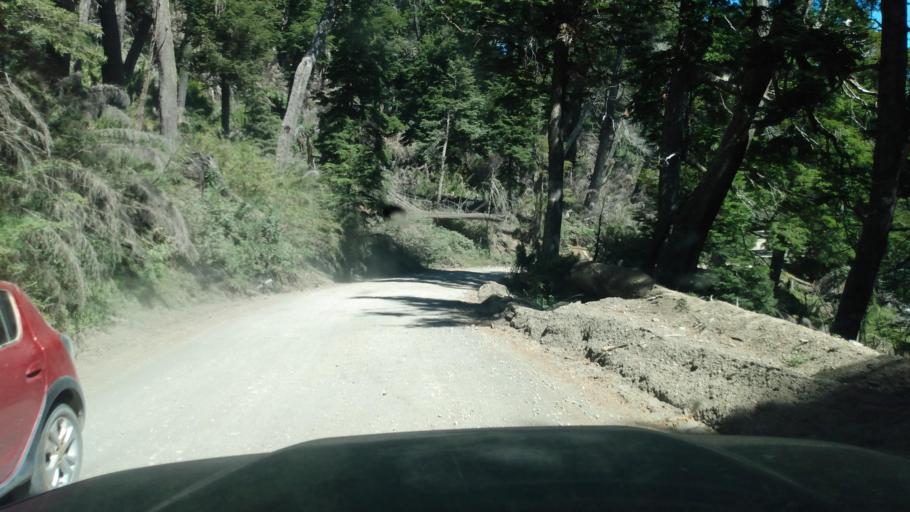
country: AR
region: Neuquen
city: Villa La Angostura
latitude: -40.6074
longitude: -71.6430
